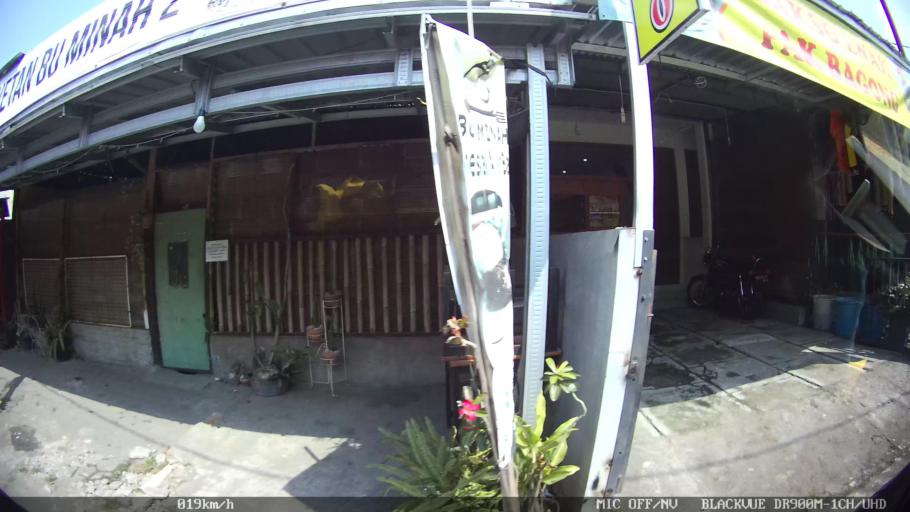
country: ID
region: Daerah Istimewa Yogyakarta
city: Yogyakarta
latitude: -7.8074
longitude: 110.3899
